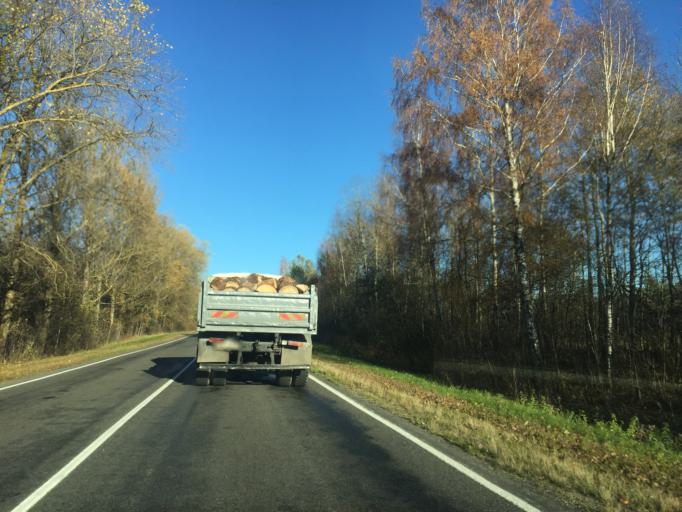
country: BY
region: Vitebsk
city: Dzisna
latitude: 55.3575
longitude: 28.3409
